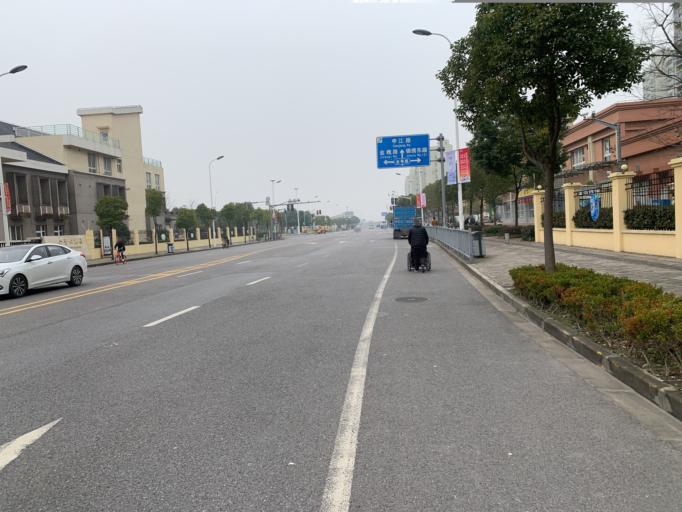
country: CN
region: Shanghai Shi
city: Huamu
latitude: 31.2414
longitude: 121.6262
